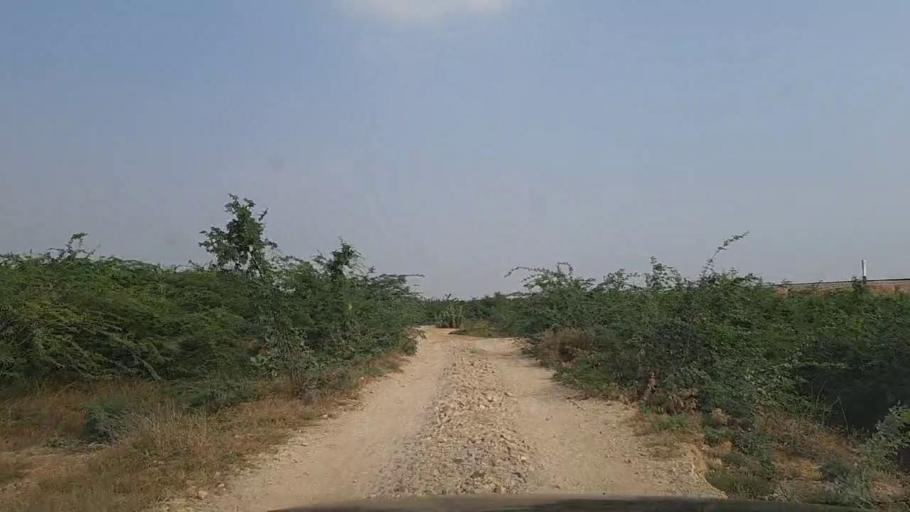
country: PK
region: Sindh
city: Thatta
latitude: 24.8636
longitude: 67.7994
